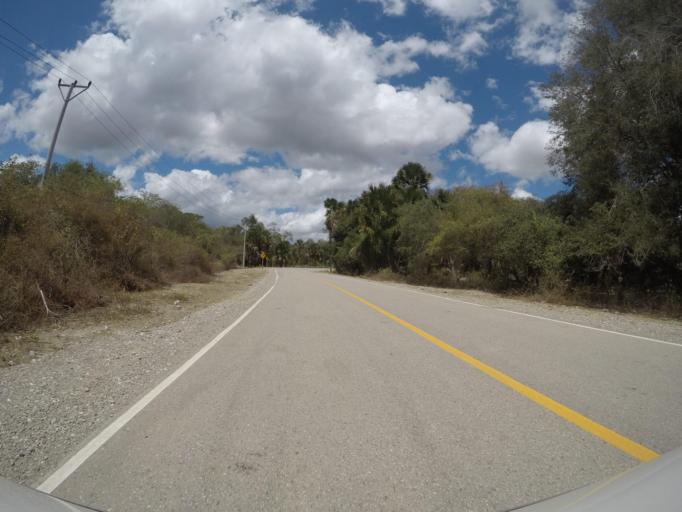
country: TL
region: Lautem
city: Lospalos
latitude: -8.4129
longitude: 126.8093
